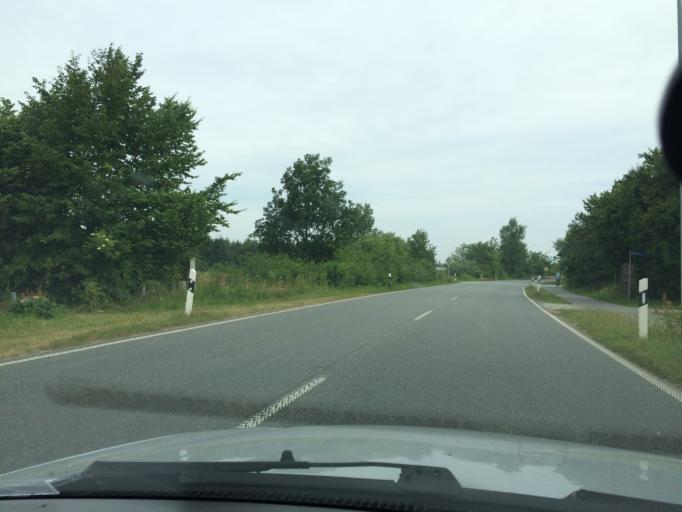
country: DE
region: Schleswig-Holstein
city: Jarplund-Weding
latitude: 54.7528
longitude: 9.4357
